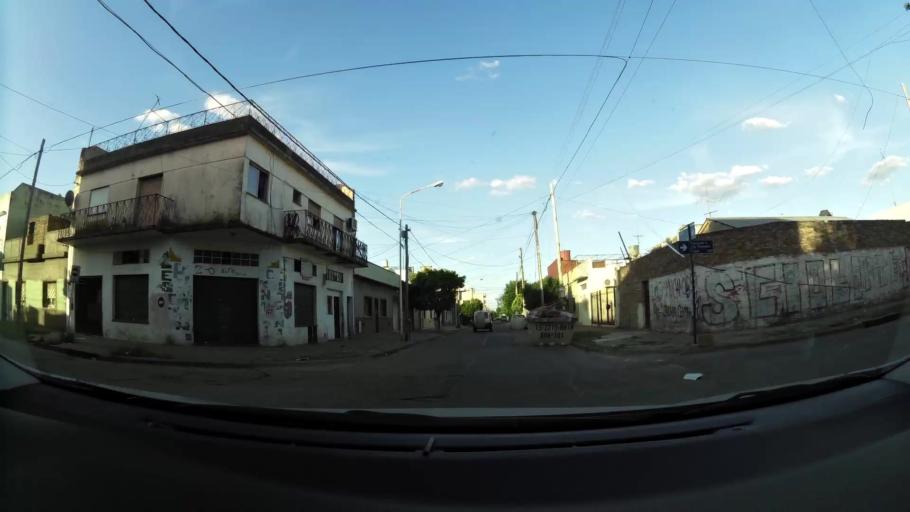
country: AR
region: Buenos Aires F.D.
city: Villa Lugano
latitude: -34.6936
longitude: -58.4884
